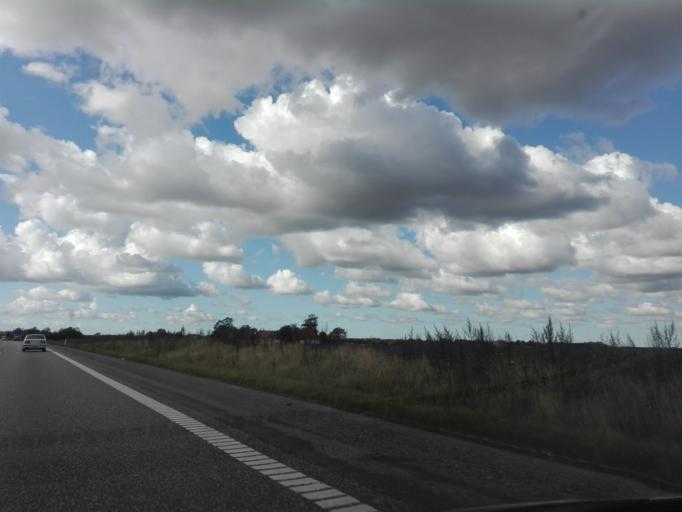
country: DK
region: North Denmark
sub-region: Mariagerfjord Kommune
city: Hobro
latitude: 56.5785
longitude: 9.8259
